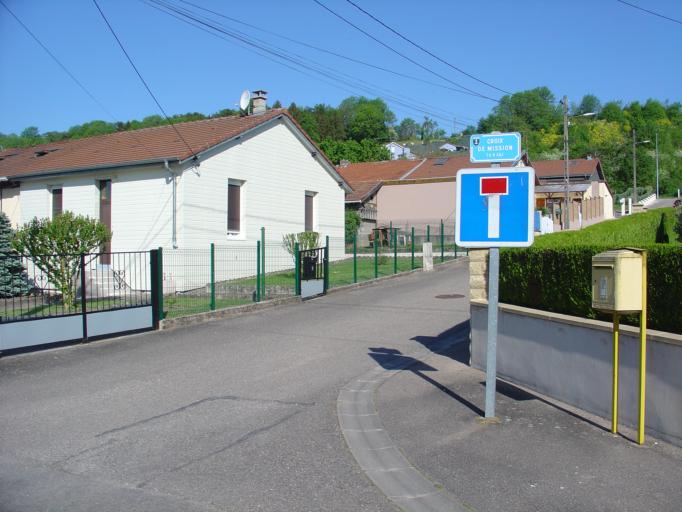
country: FR
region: Lorraine
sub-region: Departement de Meurthe-et-Moselle
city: Foug
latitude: 48.6821
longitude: 5.7837
